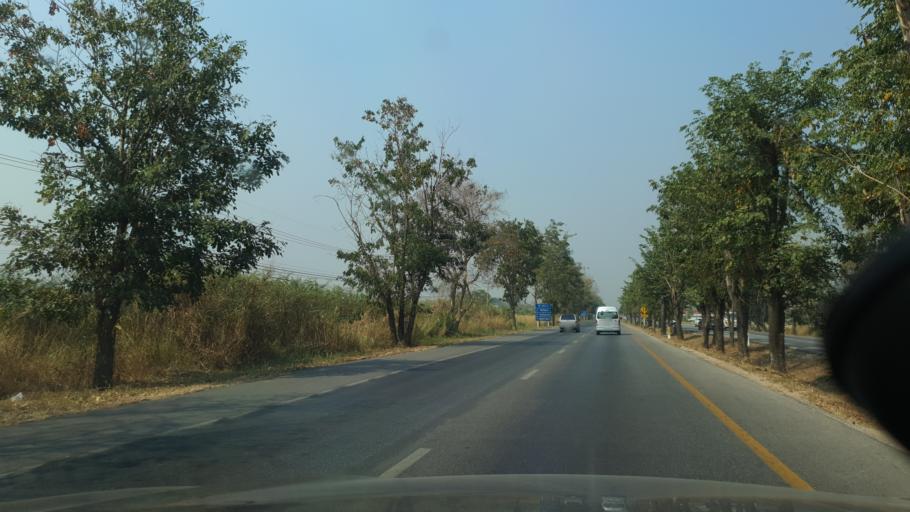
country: TH
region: Kamphaeng Phet
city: Kamphaeng Phet
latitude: 16.4321
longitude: 99.5146
